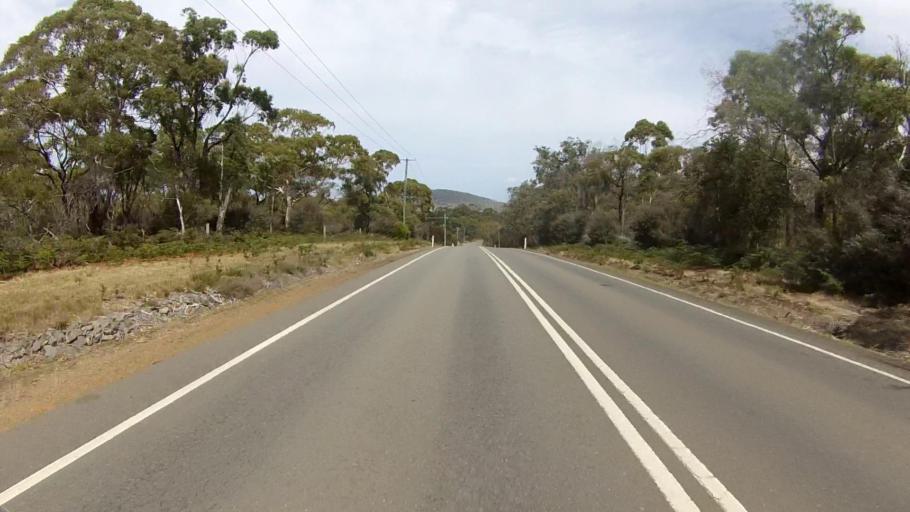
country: AU
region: Tasmania
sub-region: Clarence
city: Sandford
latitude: -43.0107
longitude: 147.4920
